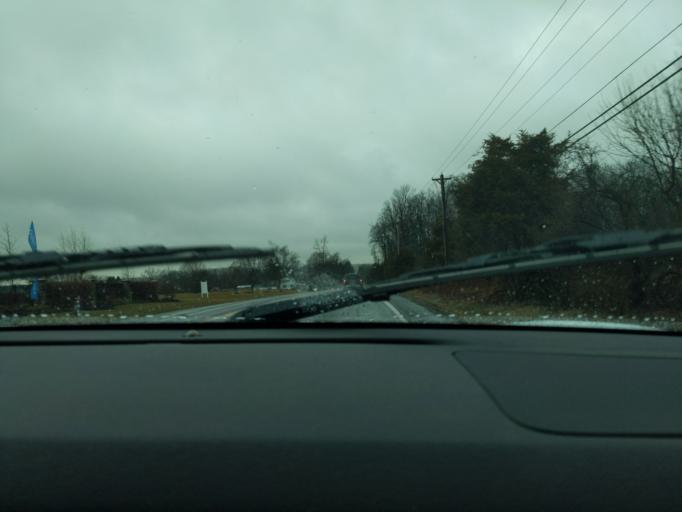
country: US
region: Pennsylvania
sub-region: Bucks County
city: Dublin
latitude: 40.3858
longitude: -75.2251
